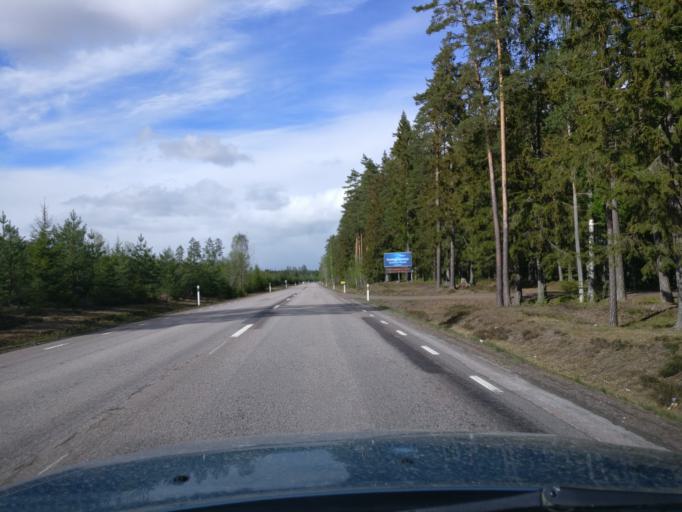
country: SE
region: Vaermland
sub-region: Forshaga Kommun
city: Forshaga
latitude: 59.5015
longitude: 13.4341
